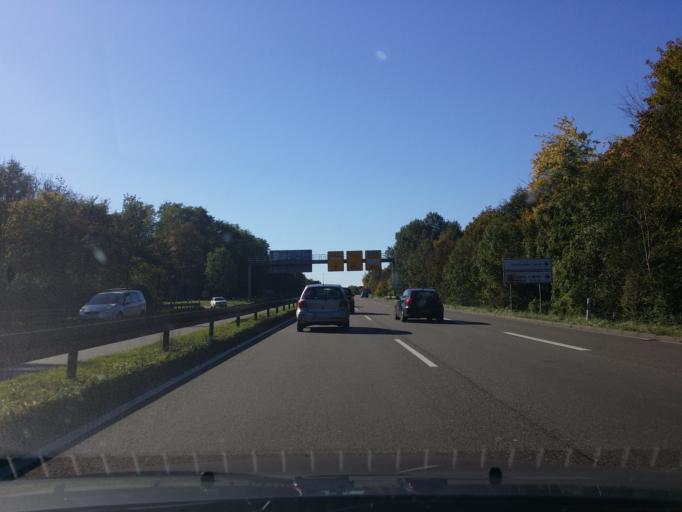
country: DE
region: Baden-Wuerttemberg
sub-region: Tuebingen Region
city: Tuebingen
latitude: 48.5141
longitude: 9.0808
